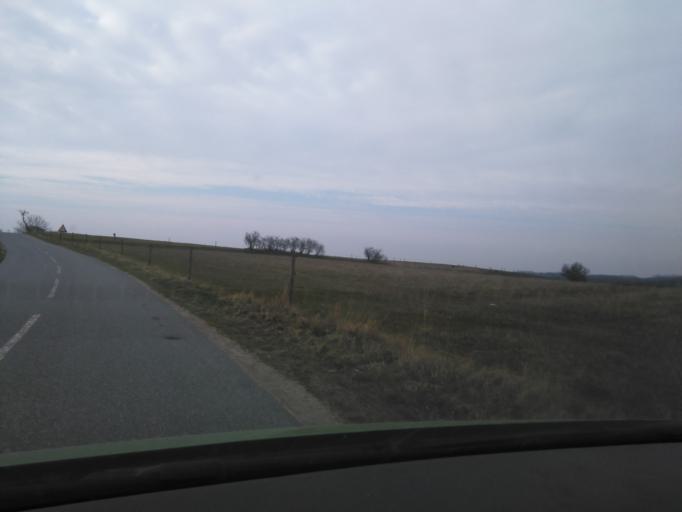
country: DK
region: Central Jutland
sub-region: Arhus Kommune
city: Beder
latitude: 56.0756
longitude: 10.2345
